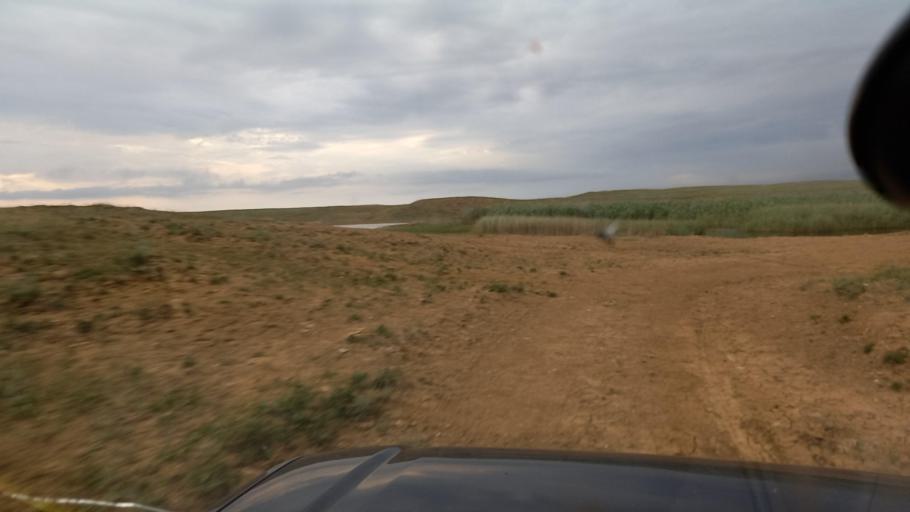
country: RU
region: Krasnodarskiy
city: Taman'
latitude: 45.2023
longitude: 36.7902
